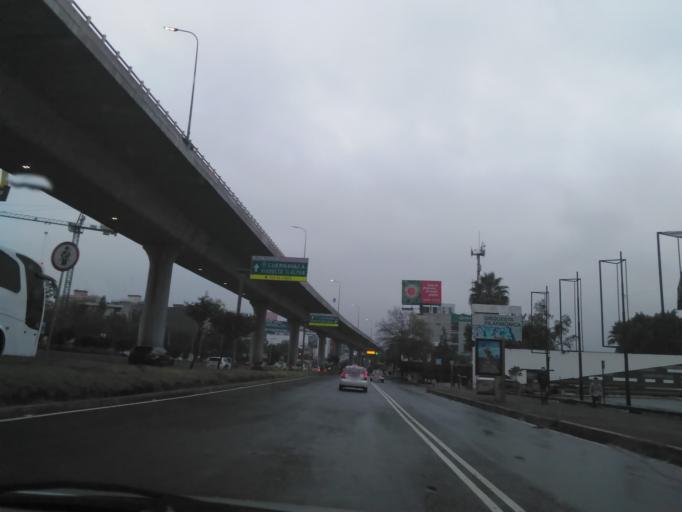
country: MX
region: Mexico City
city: Tlalpan
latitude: 19.3032
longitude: -99.1783
